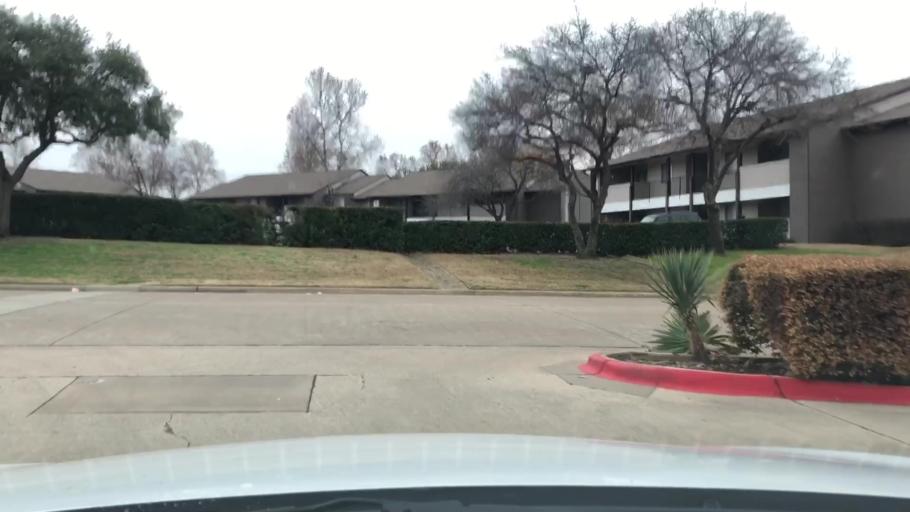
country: US
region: Texas
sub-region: Dallas County
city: Addison
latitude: 32.9639
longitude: -96.8518
